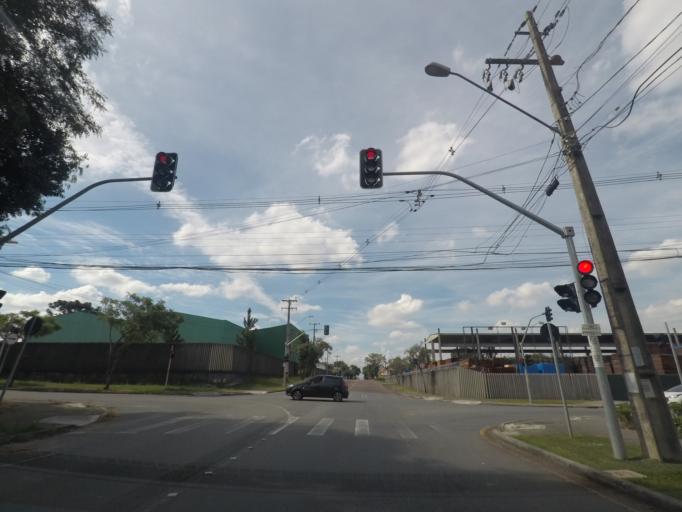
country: BR
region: Parana
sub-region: Curitiba
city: Curitiba
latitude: -25.4878
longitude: -49.2640
